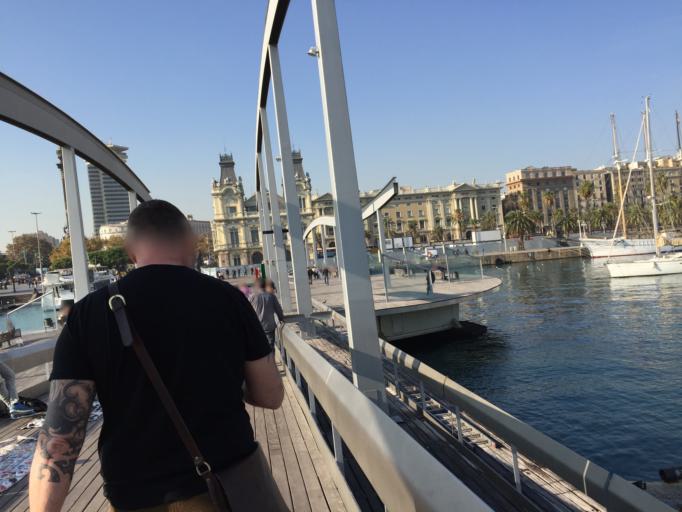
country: ES
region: Catalonia
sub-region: Provincia de Barcelona
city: Ciutat Vella
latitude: 41.3753
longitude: 2.1805
